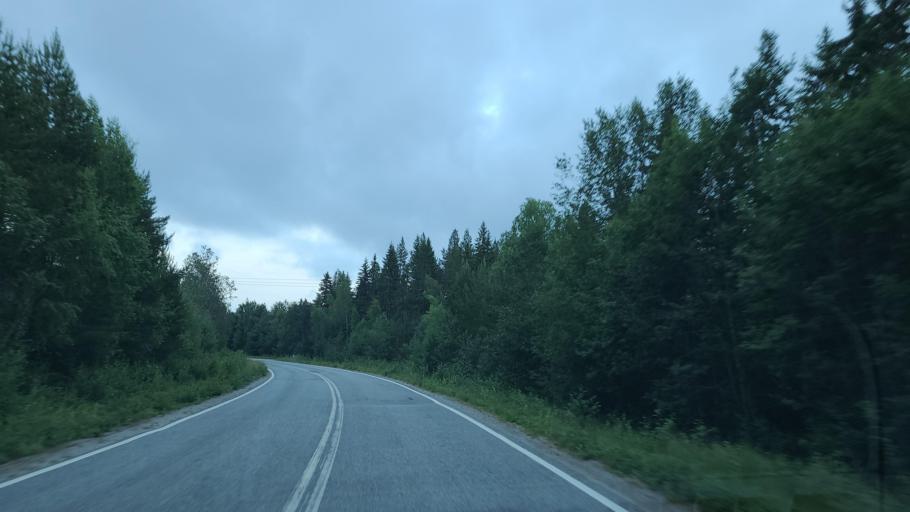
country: FI
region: Ostrobothnia
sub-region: Vaasa
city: Replot
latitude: 63.2748
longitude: 21.1387
